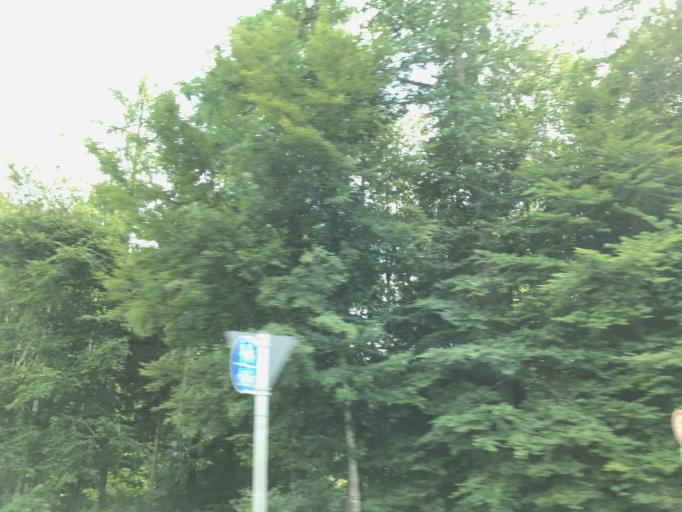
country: DE
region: Baden-Wuerttemberg
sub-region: Tuebingen Region
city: Wangen im Allgau
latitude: 47.7044
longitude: 9.8189
